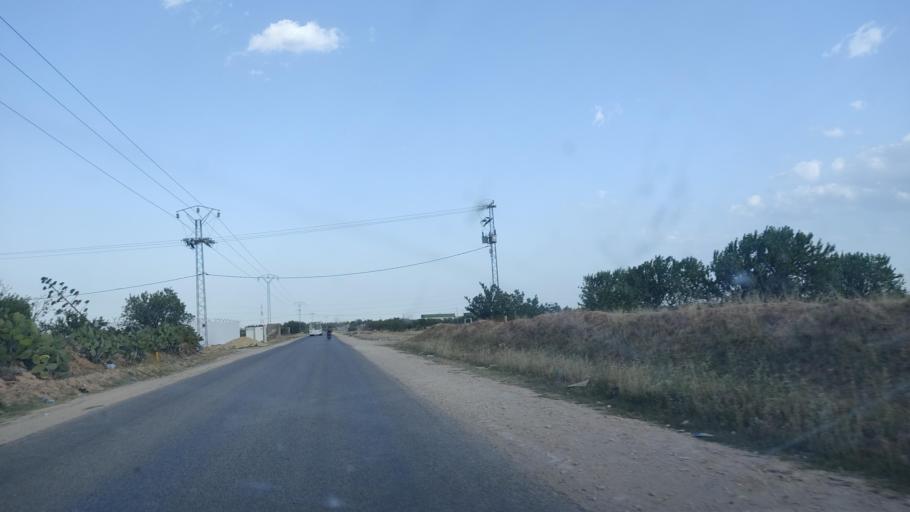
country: TN
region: Safaqis
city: Sfax
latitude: 34.8374
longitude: 10.6281
